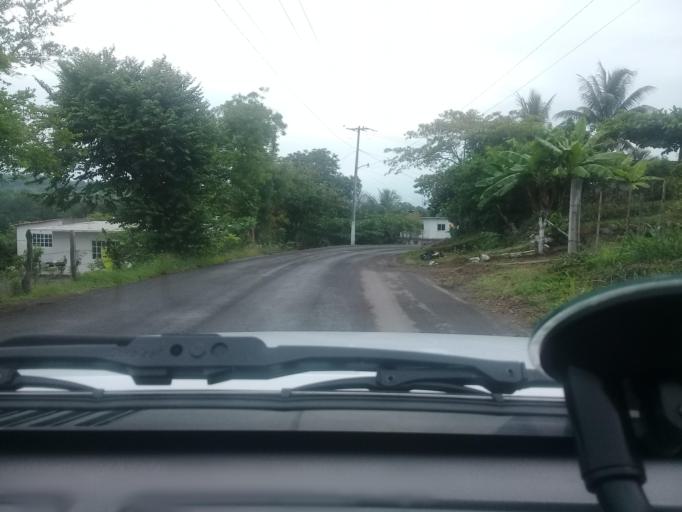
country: MX
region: Veracruz
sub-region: Paso de Ovejas
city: Tolome
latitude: 19.2611
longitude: -96.4136
